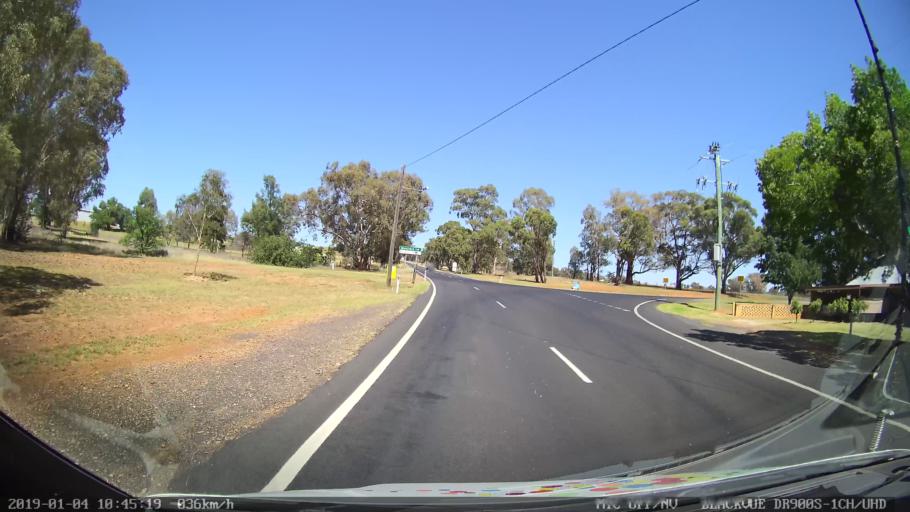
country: AU
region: New South Wales
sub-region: Cabonne
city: Molong
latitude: -33.2893
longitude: 148.7277
